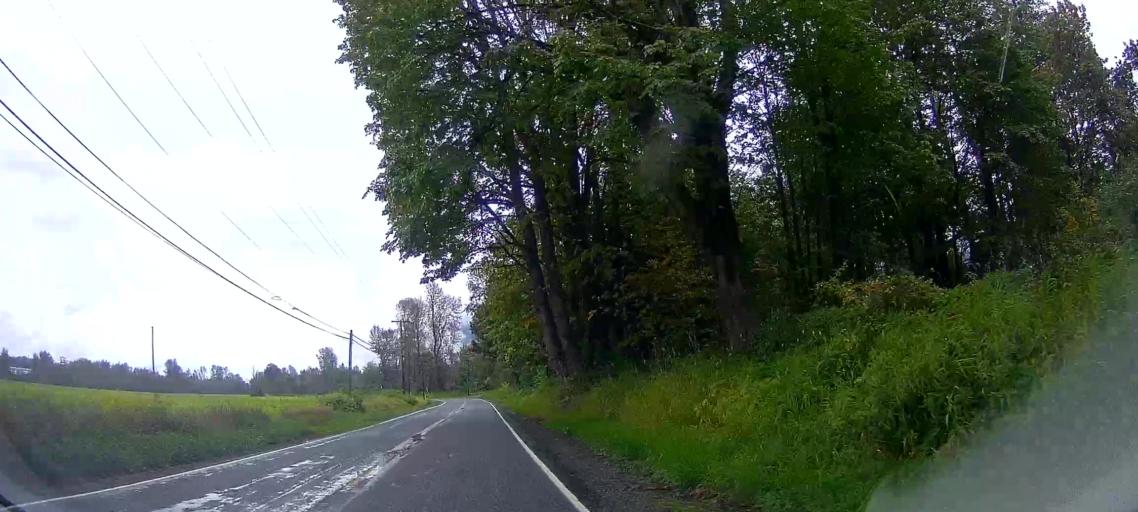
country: US
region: Washington
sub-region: Skagit County
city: Sedro-Woolley
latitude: 48.5270
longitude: -122.0182
